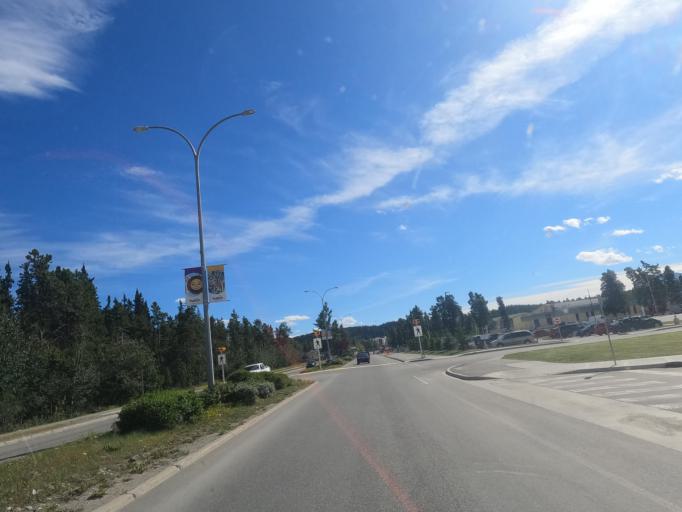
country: CA
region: Yukon
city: Whitehorse
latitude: 60.7103
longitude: -135.0381
